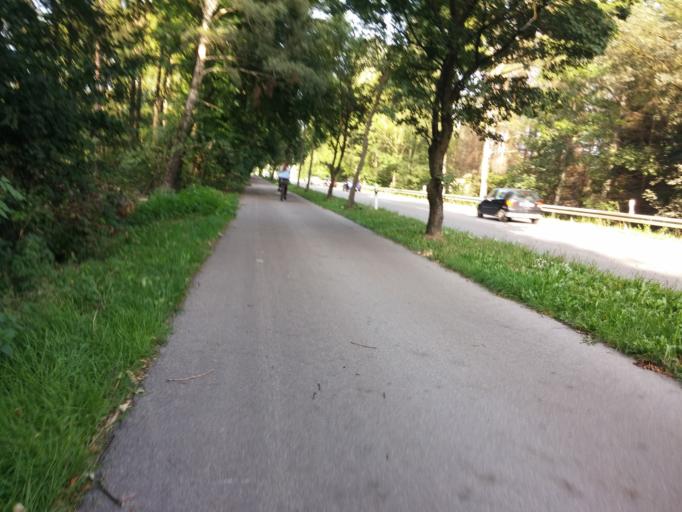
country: DE
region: Bavaria
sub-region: Swabia
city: Memmingen
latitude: 47.9812
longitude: 10.1950
